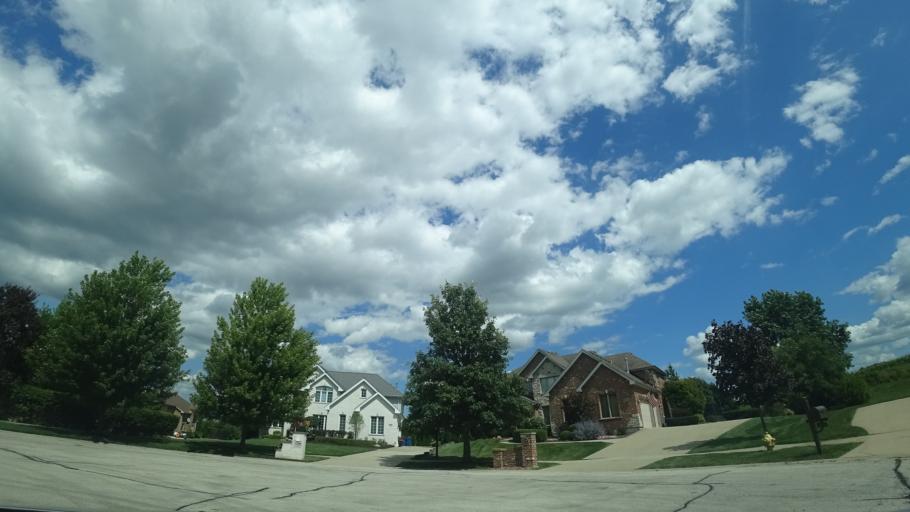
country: US
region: Illinois
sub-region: Will County
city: Homer Glen
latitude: 41.5893
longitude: -87.9069
